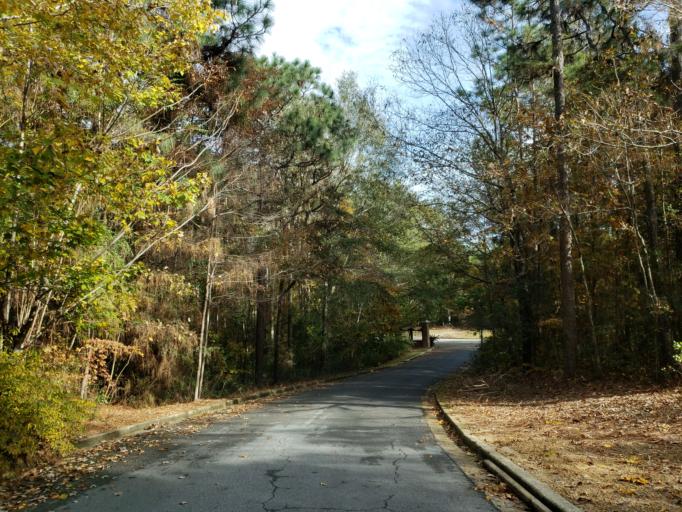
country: US
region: Mississippi
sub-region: Lamar County
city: West Hattiesburg
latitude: 31.3211
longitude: -89.4727
